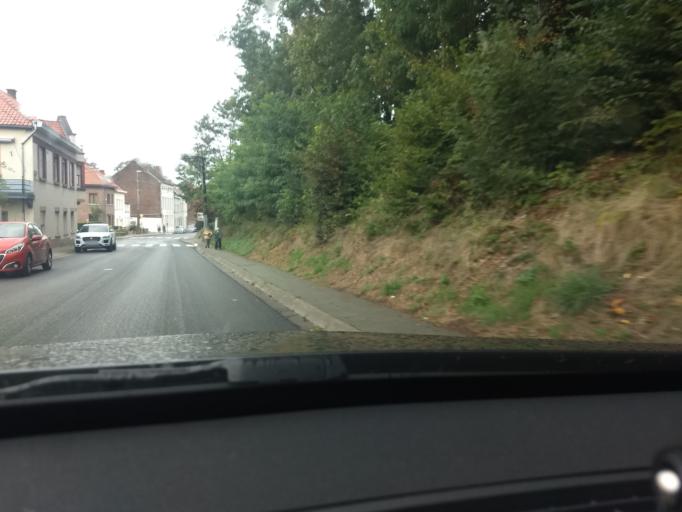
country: BE
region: Wallonia
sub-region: Province du Brabant Wallon
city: Braine-l'Alleud
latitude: 50.6795
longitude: 4.3706
